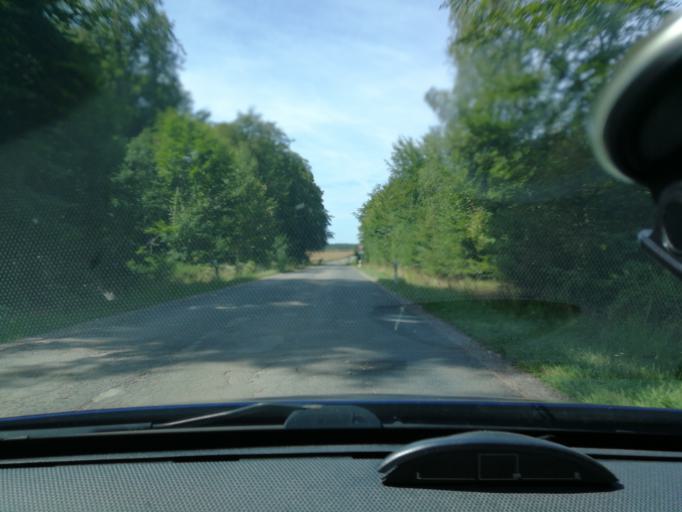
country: DE
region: Rheinland-Pfalz
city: Dodenburg
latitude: 49.9188
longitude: 6.7884
